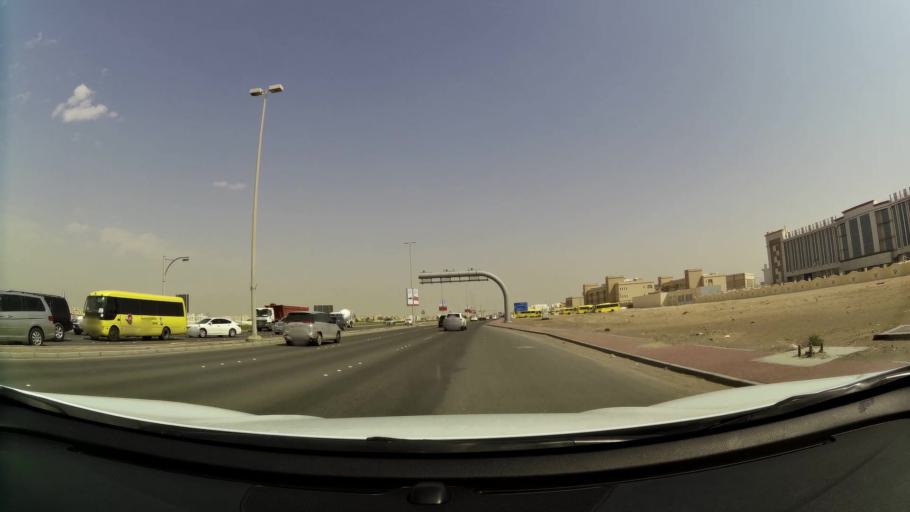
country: AE
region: Abu Dhabi
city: Abu Dhabi
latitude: 24.3472
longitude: 54.5383
